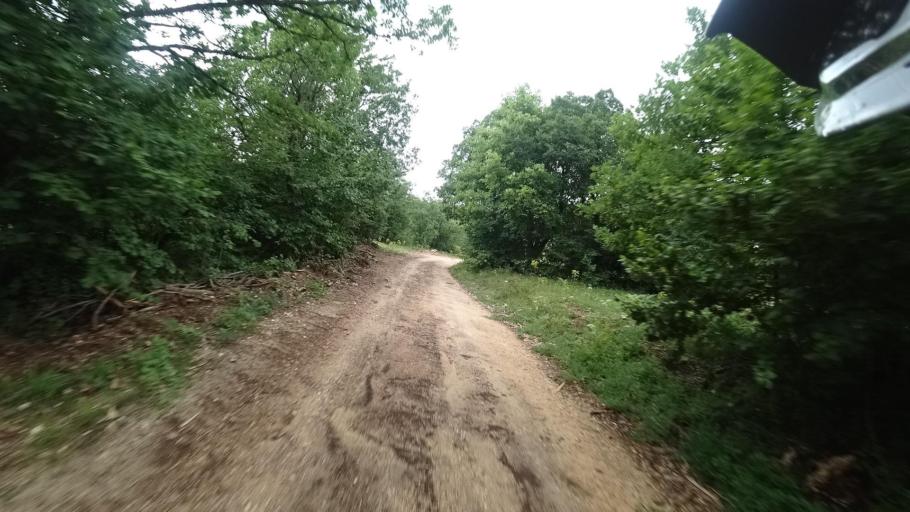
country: BA
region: Federation of Bosnia and Herzegovina
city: Bihac
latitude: 44.6675
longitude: 15.7504
